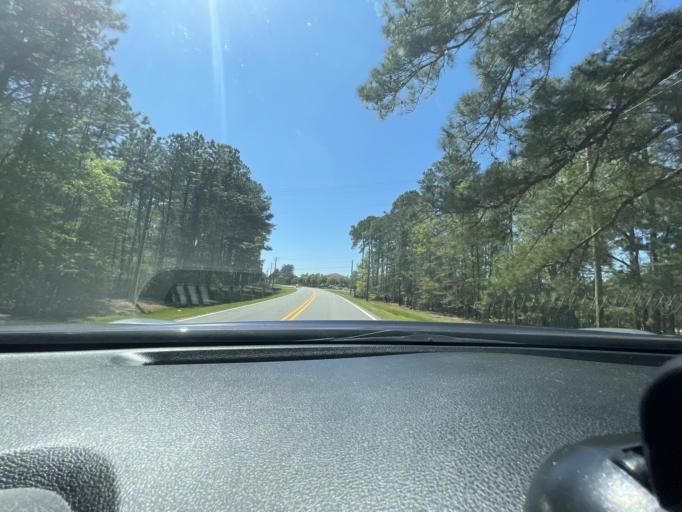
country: US
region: Georgia
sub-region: Chatham County
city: Bloomingdale
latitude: 32.1006
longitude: -81.2844
